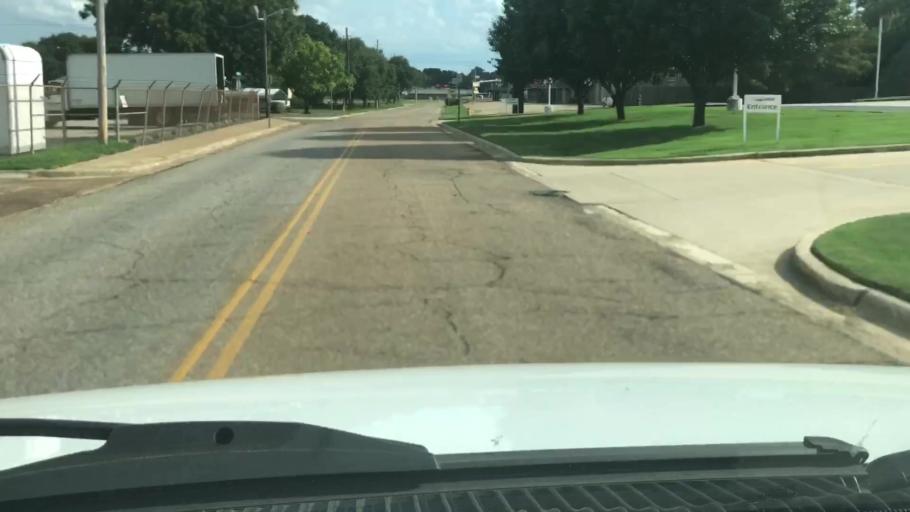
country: US
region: Texas
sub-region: Bowie County
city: Wake Village
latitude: 33.4396
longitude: -94.0826
